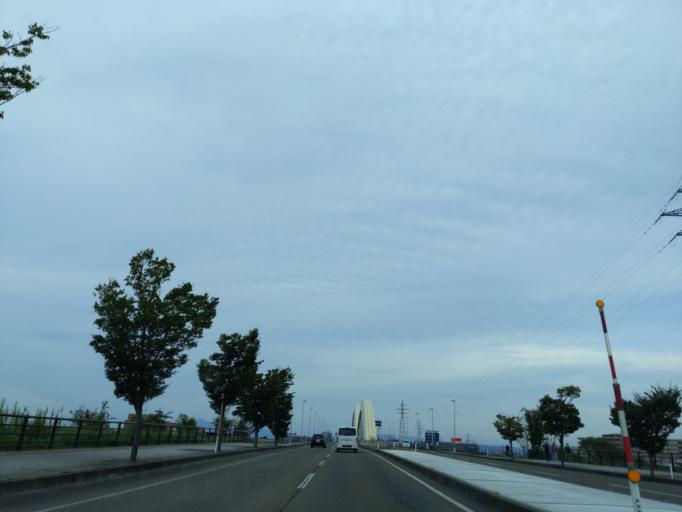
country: JP
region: Niigata
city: Joetsu
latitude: 37.1494
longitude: 138.2419
